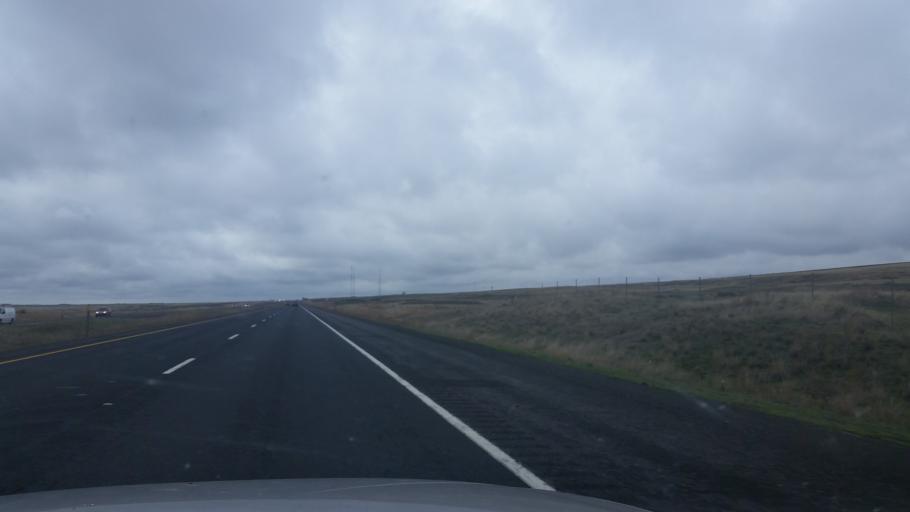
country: US
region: Washington
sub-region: Spokane County
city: Medical Lake
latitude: 47.3285
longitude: -117.9293
